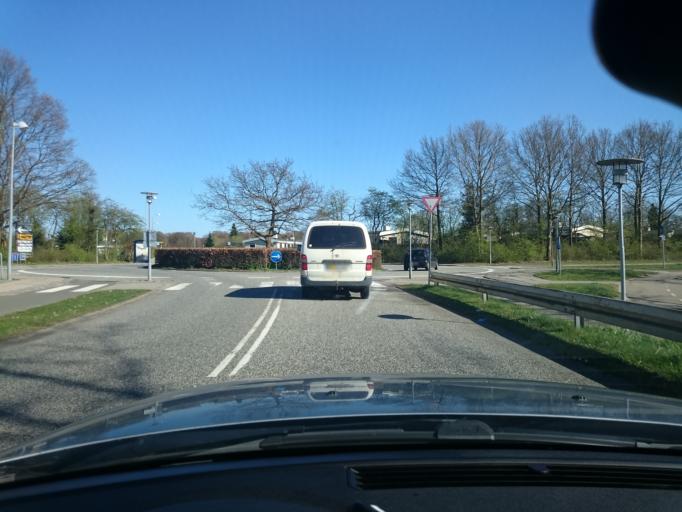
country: DK
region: Capital Region
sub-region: Lyngby-Tarbaek Kommune
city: Kongens Lyngby
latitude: 55.7952
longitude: 12.5359
